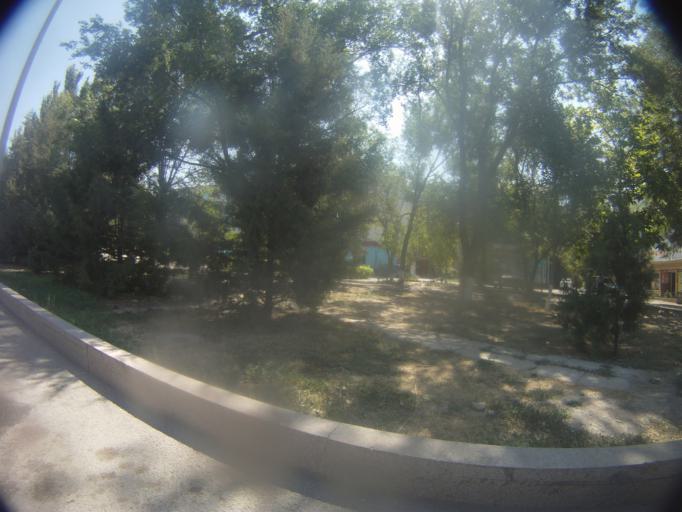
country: KZ
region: Zhambyl
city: Taraz
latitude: 42.8855
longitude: 71.3070
